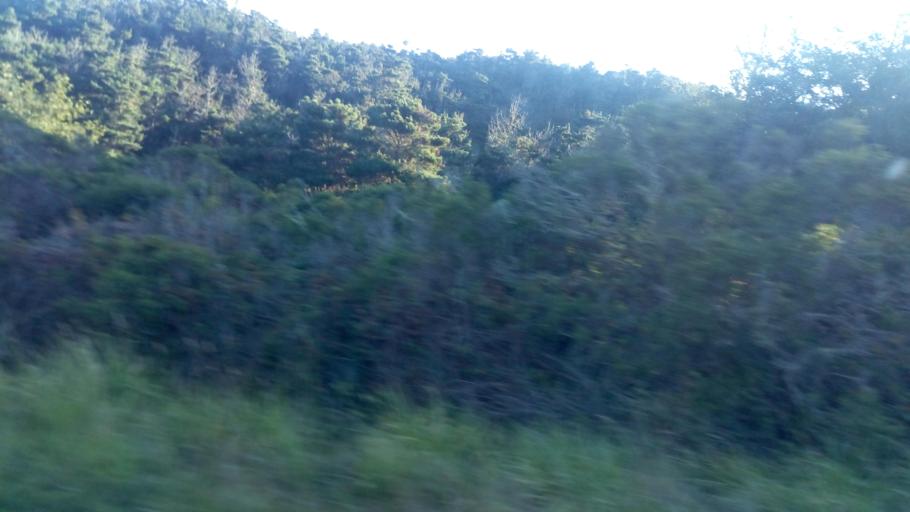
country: US
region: California
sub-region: Marin County
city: Inverness
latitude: 38.0448
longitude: -122.8660
